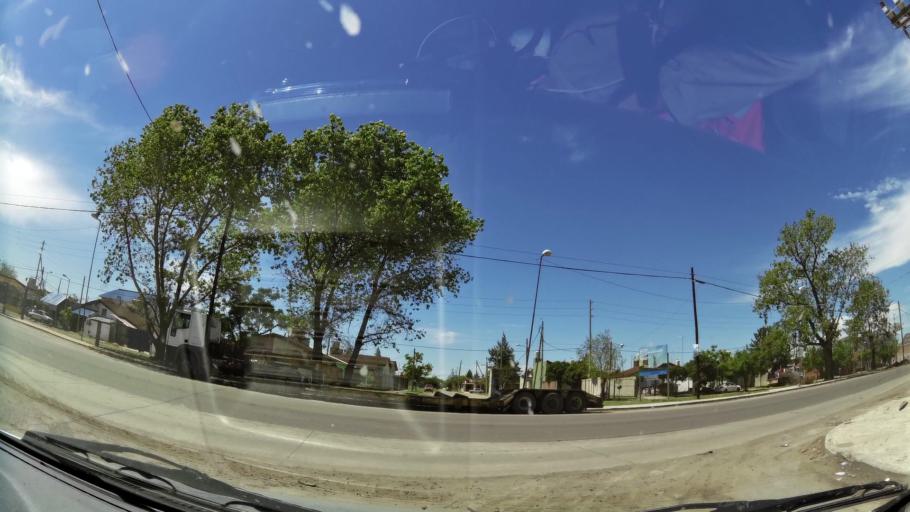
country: AR
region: Buenos Aires
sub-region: Partido de Quilmes
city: Quilmes
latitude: -34.7483
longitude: -58.3091
